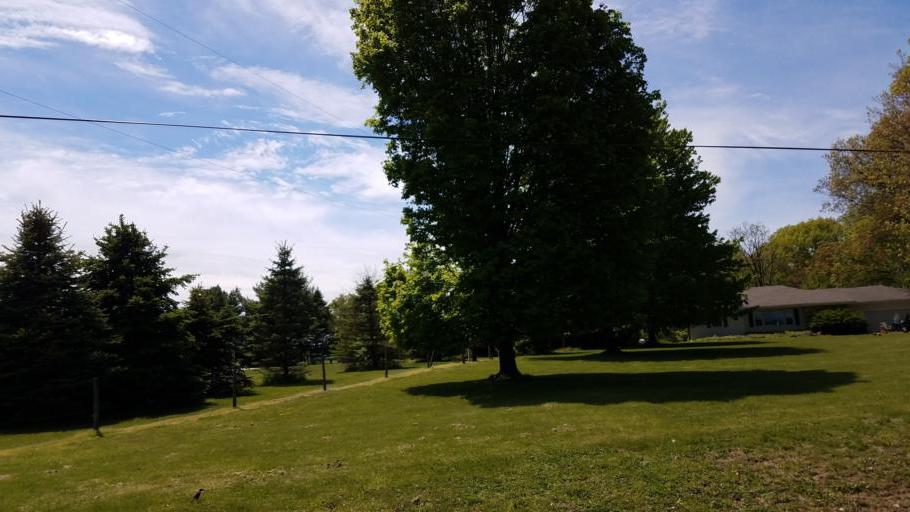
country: US
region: Ohio
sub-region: Knox County
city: Gambier
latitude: 40.3961
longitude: -82.4080
